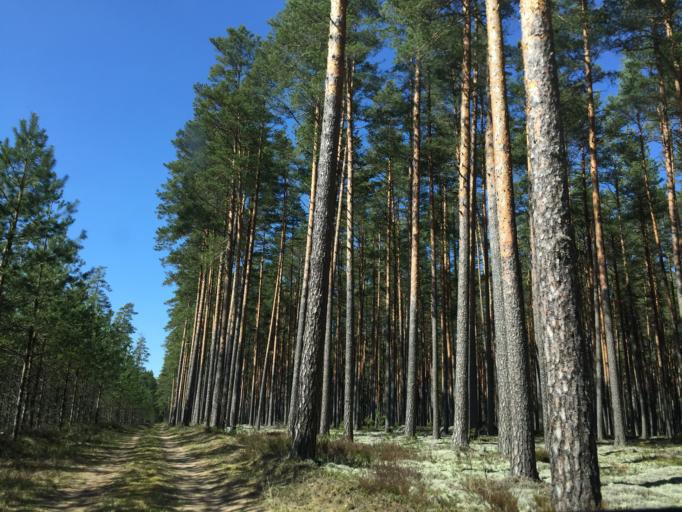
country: LV
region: Strenci
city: Strenci
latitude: 57.5932
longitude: 25.7141
